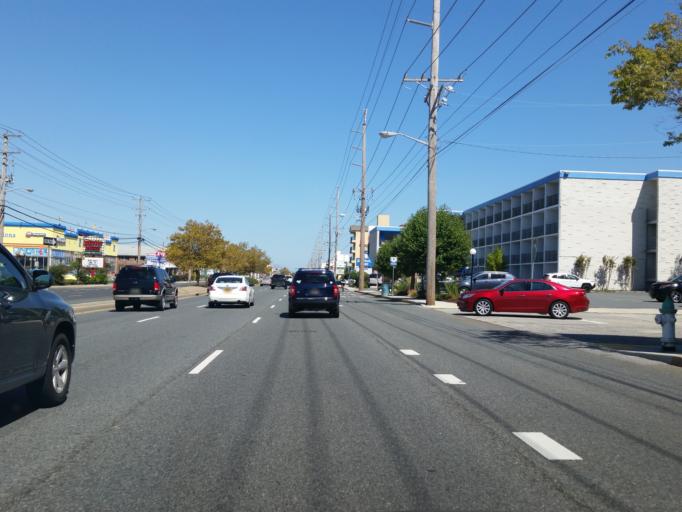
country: US
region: Maryland
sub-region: Worcester County
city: Ocean City
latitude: 38.4291
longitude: -75.0551
